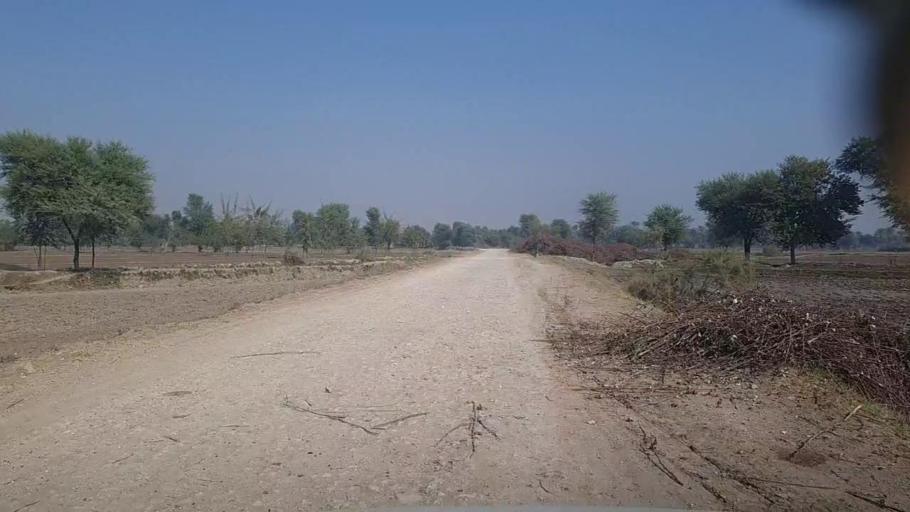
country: PK
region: Sindh
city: Kandiari
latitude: 26.9341
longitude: 68.5275
